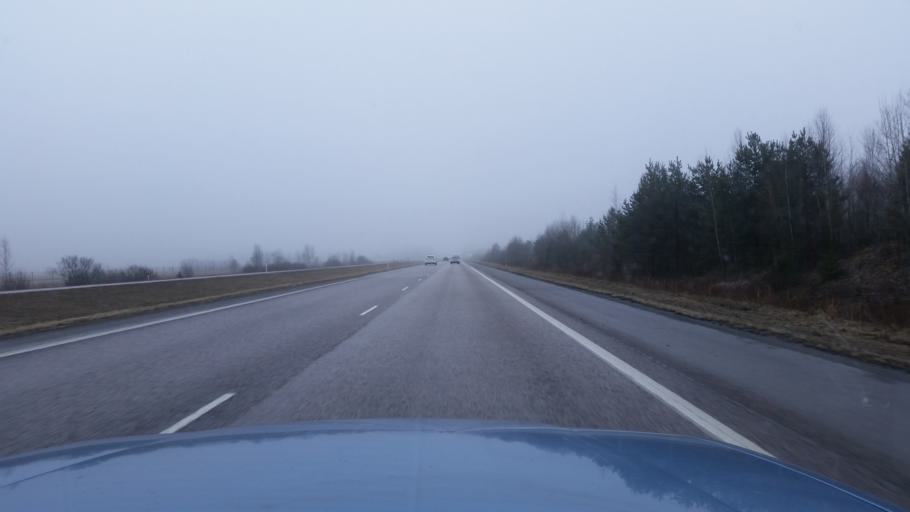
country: FI
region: Uusimaa
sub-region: Helsinki
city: Nurmijaervi
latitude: 60.5306
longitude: 24.8421
